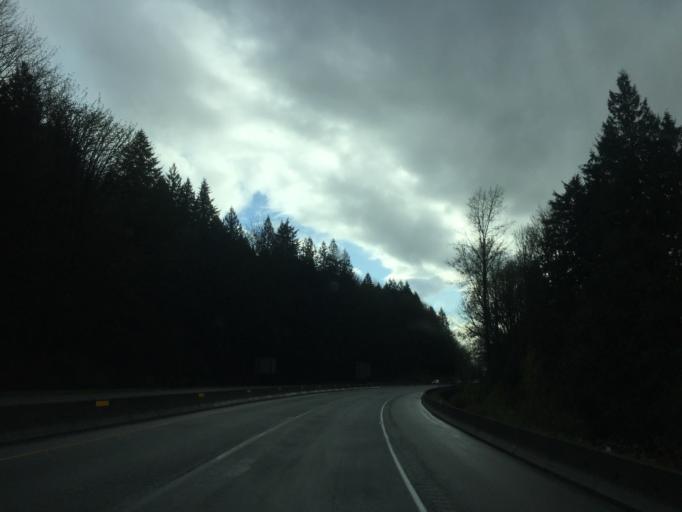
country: CA
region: British Columbia
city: Agassiz
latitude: 49.1732
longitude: -121.7767
